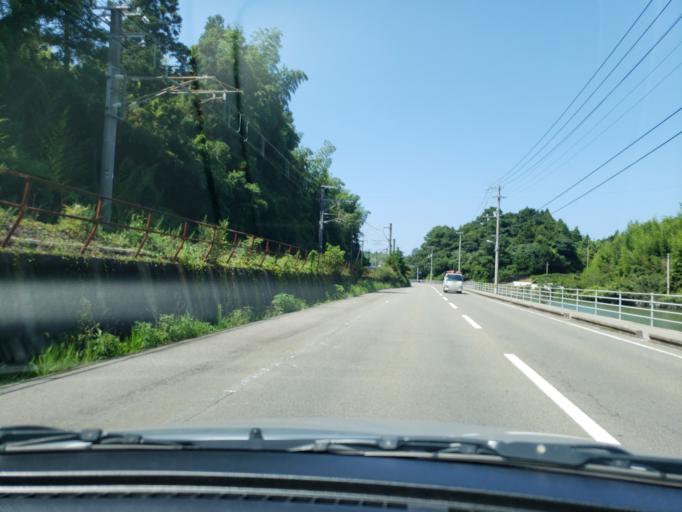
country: JP
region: Ehime
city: Hojo
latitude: 34.0948
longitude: 132.9363
